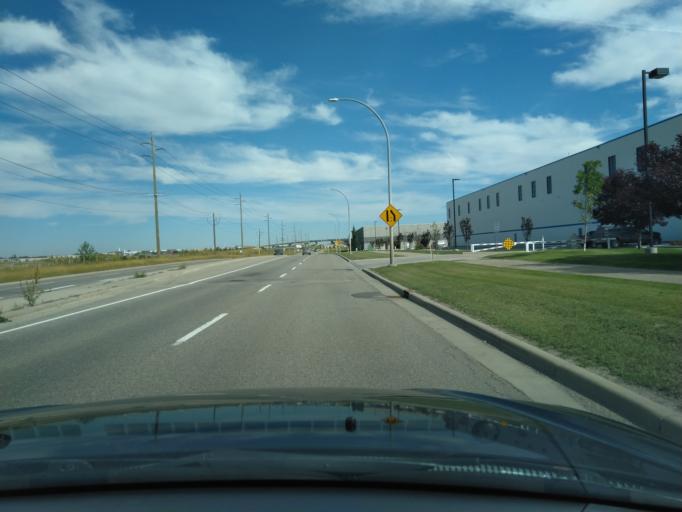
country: CA
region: Alberta
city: Calgary
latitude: 51.0959
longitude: -113.9974
